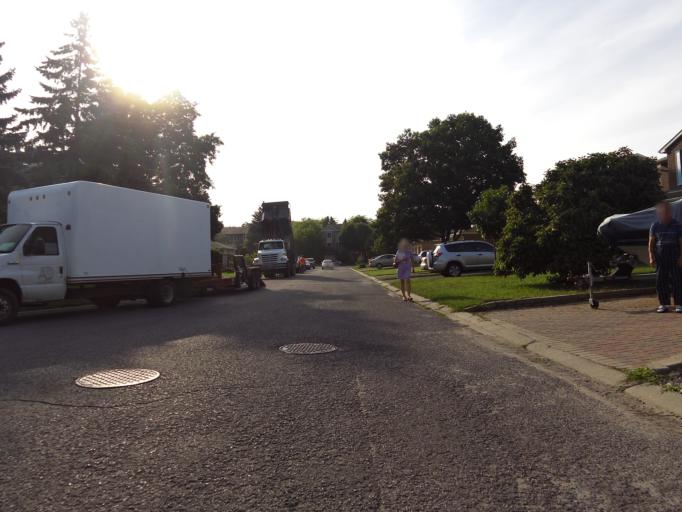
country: CA
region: Ontario
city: Bells Corners
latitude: 45.3392
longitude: -75.7605
